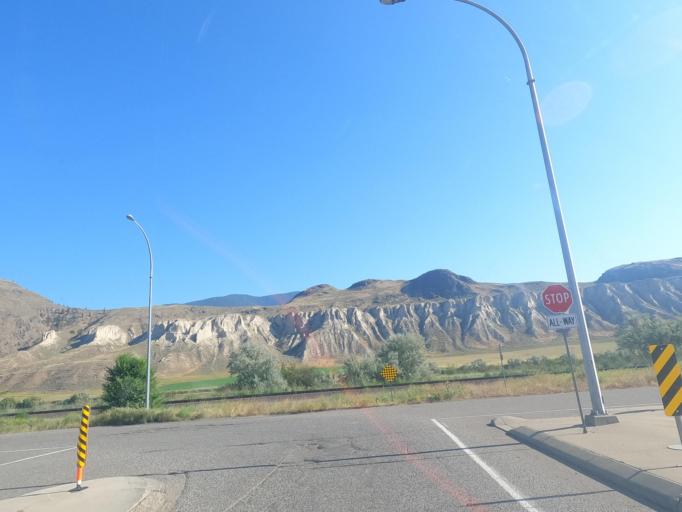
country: CA
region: British Columbia
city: Kamloops
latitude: 50.6612
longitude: -120.1180
